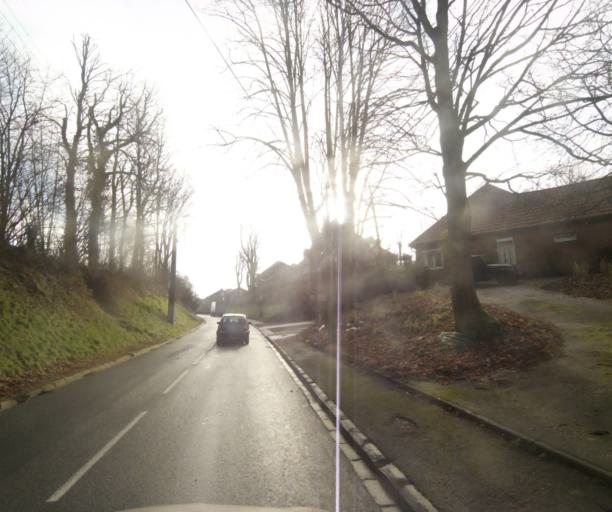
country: FR
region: Nord-Pas-de-Calais
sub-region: Departement du Nord
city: Artres
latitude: 50.2893
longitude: 3.5422
